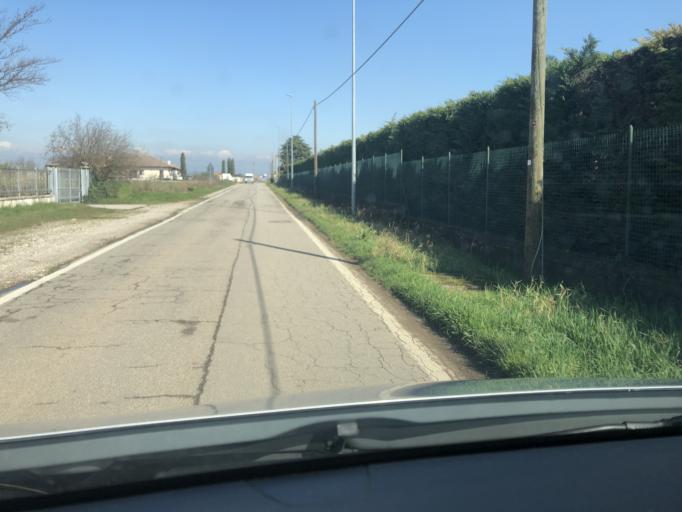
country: IT
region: Veneto
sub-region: Provincia di Verona
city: Villafranca di Verona
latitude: 45.3715
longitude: 10.8285
